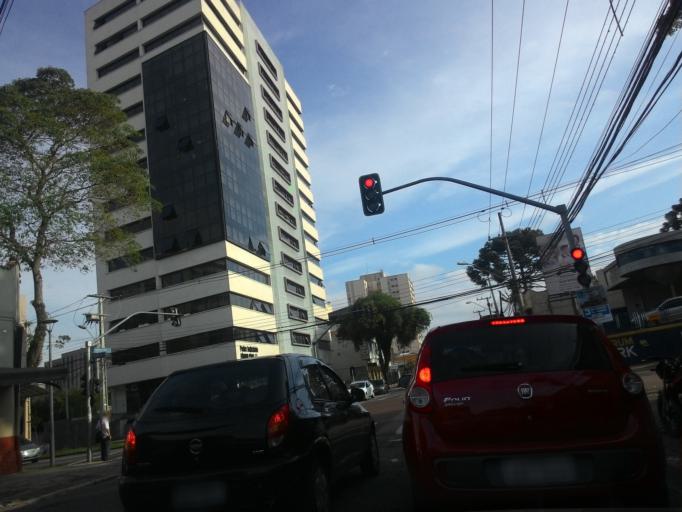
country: BR
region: Parana
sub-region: Curitiba
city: Curitiba
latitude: -25.4168
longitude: -49.2716
